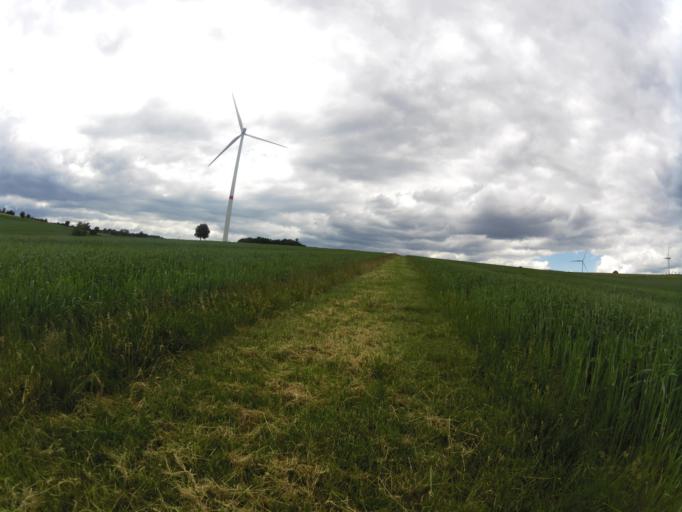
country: DE
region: Bavaria
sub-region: Regierungsbezirk Unterfranken
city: Guntersleben
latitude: 49.8838
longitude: 9.8838
